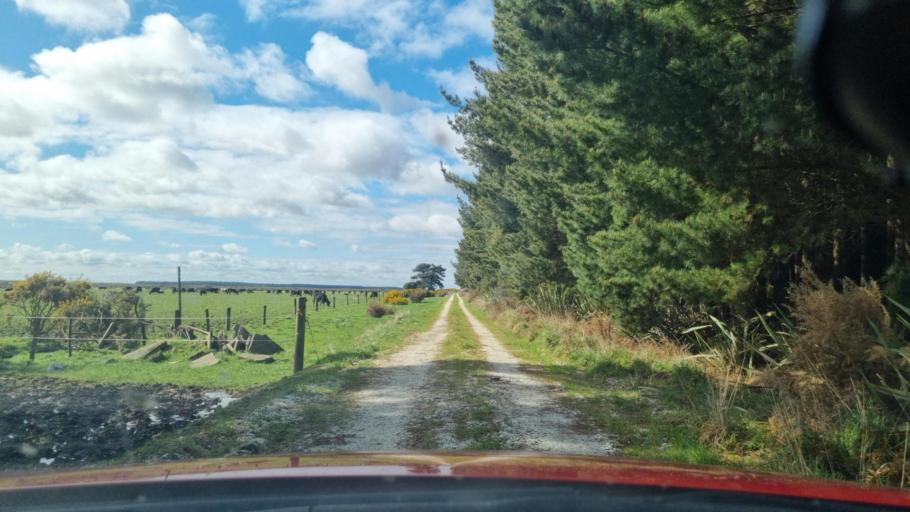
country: NZ
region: Southland
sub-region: Invercargill City
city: Invercargill
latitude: -46.4920
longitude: 168.4398
